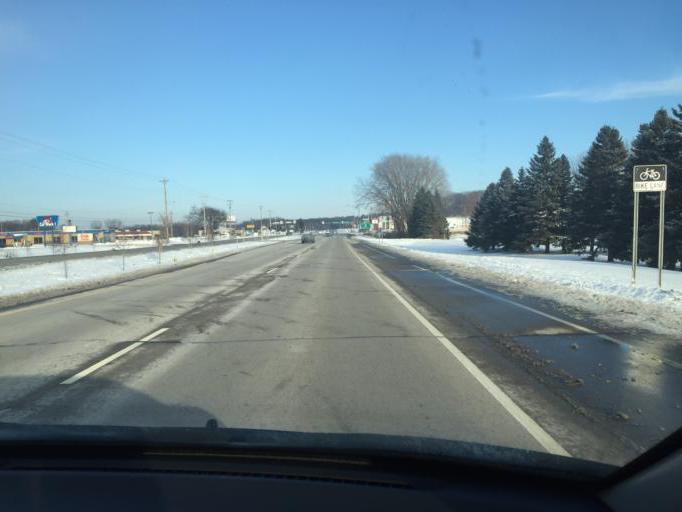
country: US
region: Minnesota
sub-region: Olmsted County
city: Rochester
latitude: 44.0078
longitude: -92.4451
